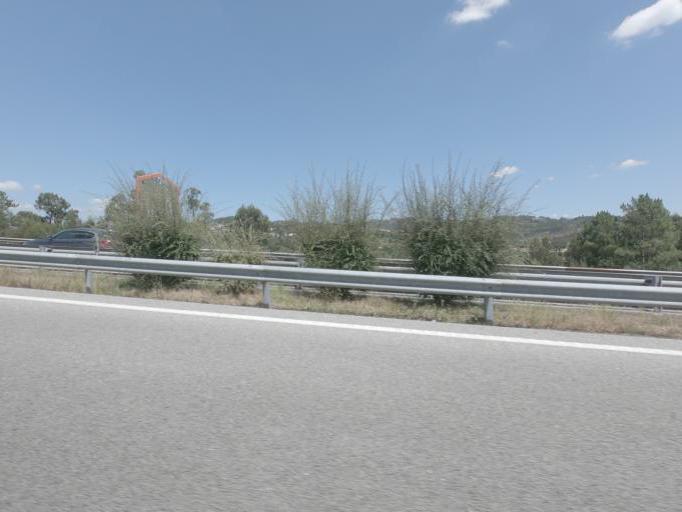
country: PT
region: Porto
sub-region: Marco de Canaveses
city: Marco de Canavezes
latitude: 41.2326
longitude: -8.1775
